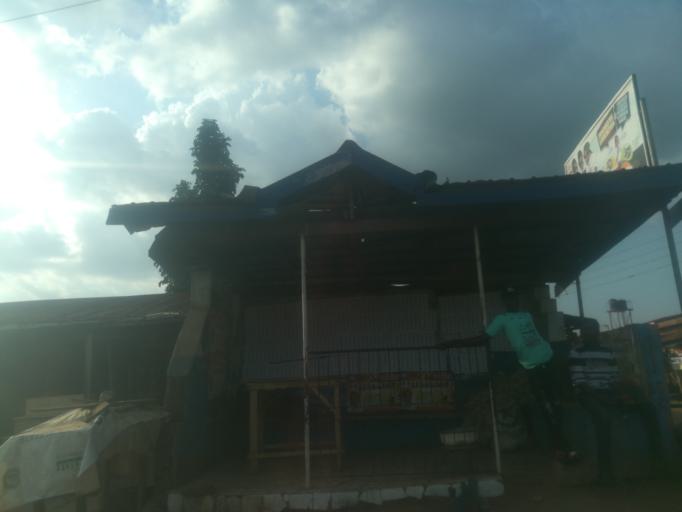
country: NG
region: Ogun
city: Abeokuta
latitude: 7.1219
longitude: 3.3212
